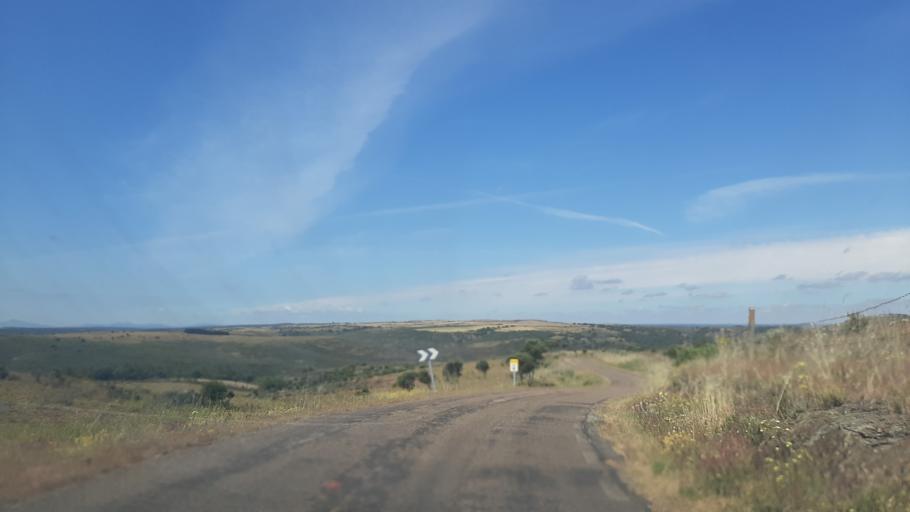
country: ES
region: Castille and Leon
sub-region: Provincia de Salamanca
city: Zamarra
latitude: 40.5252
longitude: -6.4612
